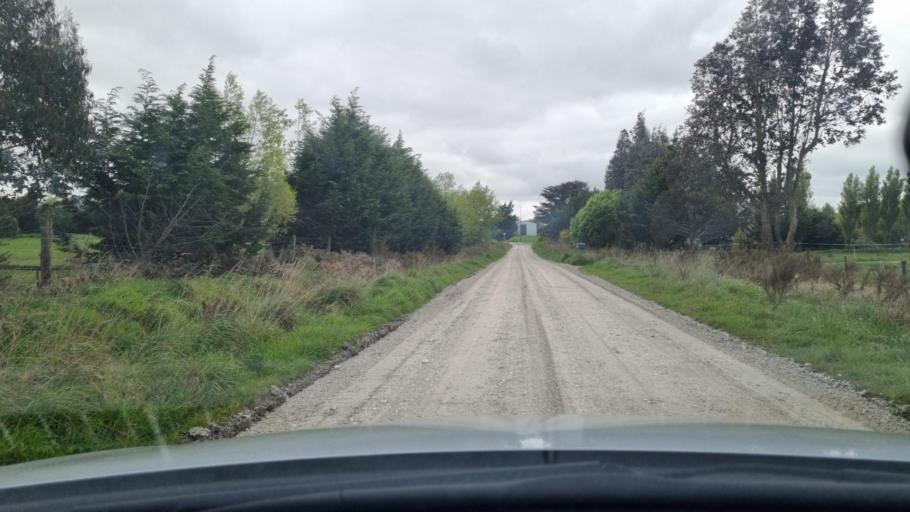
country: NZ
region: Southland
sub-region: Invercargill City
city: Invercargill
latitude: -46.4340
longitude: 168.3896
